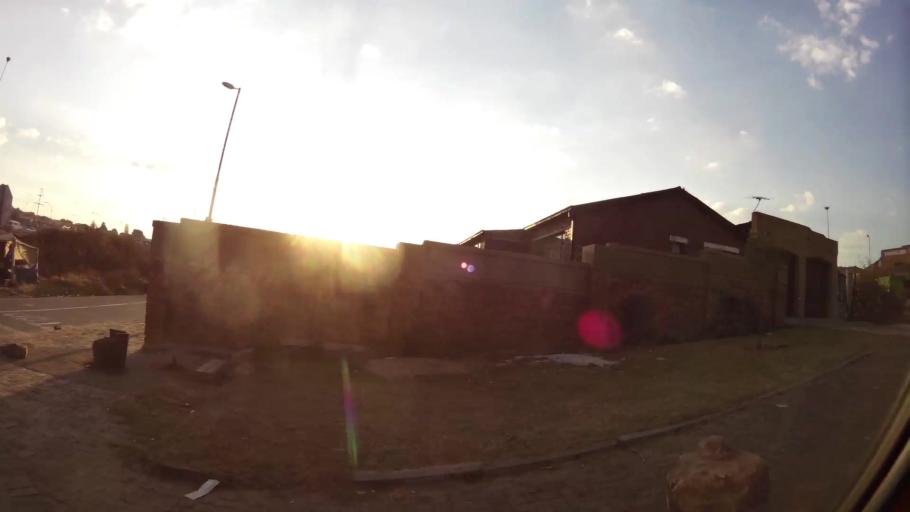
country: ZA
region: Gauteng
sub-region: City of Johannesburg Metropolitan Municipality
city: Soweto
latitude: -26.2277
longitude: 27.9068
